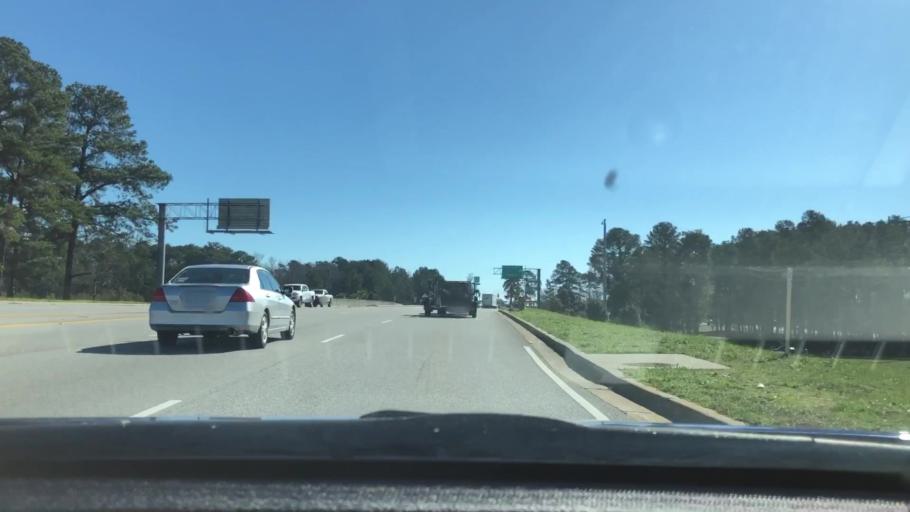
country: US
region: South Carolina
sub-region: Lexington County
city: Oak Grove
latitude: 34.0121
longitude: -81.1496
